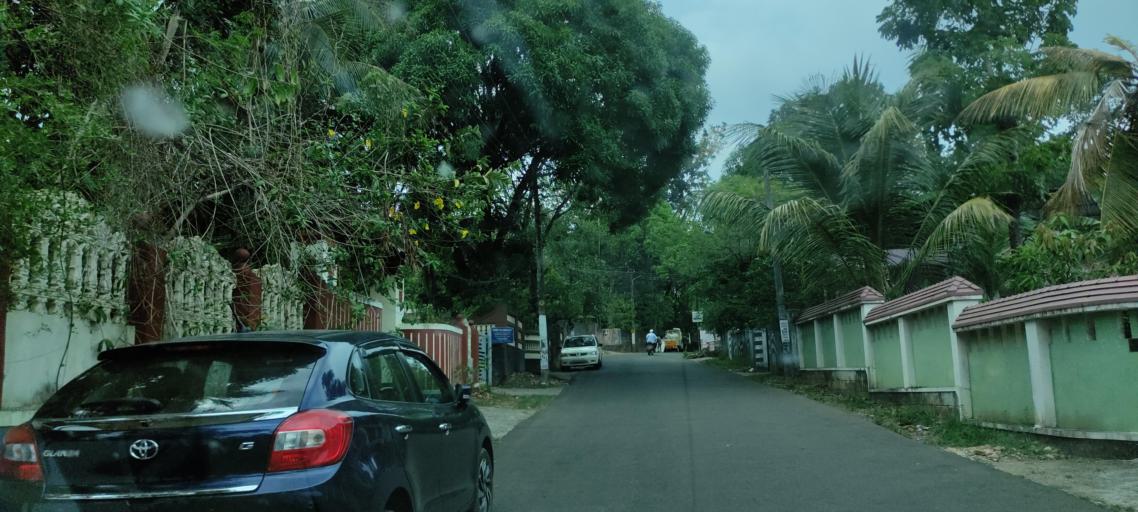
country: IN
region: Kerala
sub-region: Pattanamtitta
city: Adur
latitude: 9.1643
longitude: 76.7352
